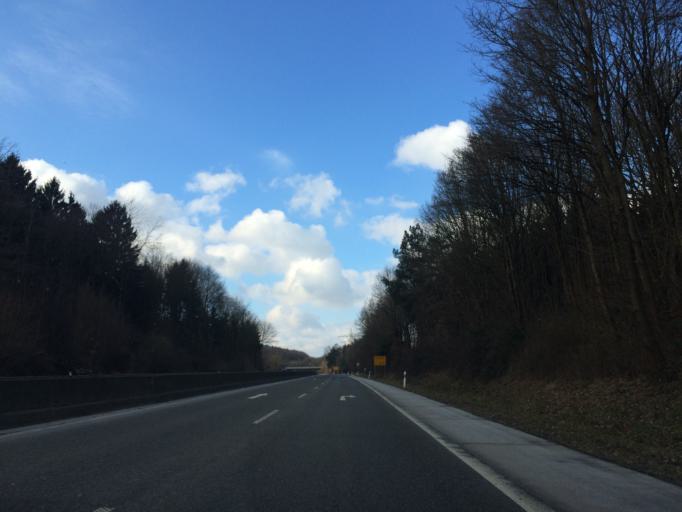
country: DE
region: Hesse
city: Kelkheim (Taunus)
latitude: 50.1496
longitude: 8.4667
